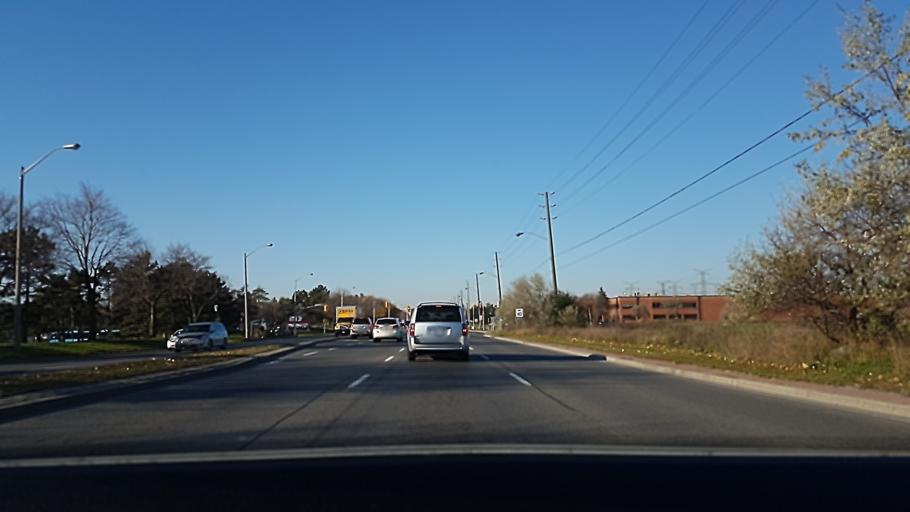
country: CA
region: Ontario
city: Concord
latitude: 43.7798
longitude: -79.5024
